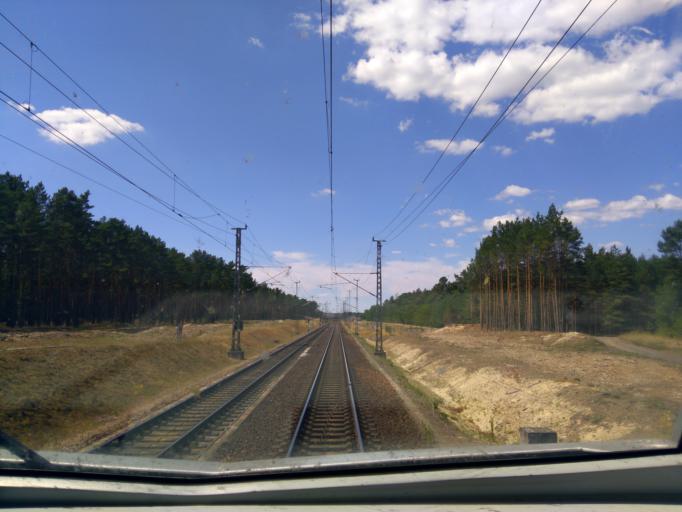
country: DE
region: Saxony-Anhalt
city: Havelberg
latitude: 52.9002
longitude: 12.0992
